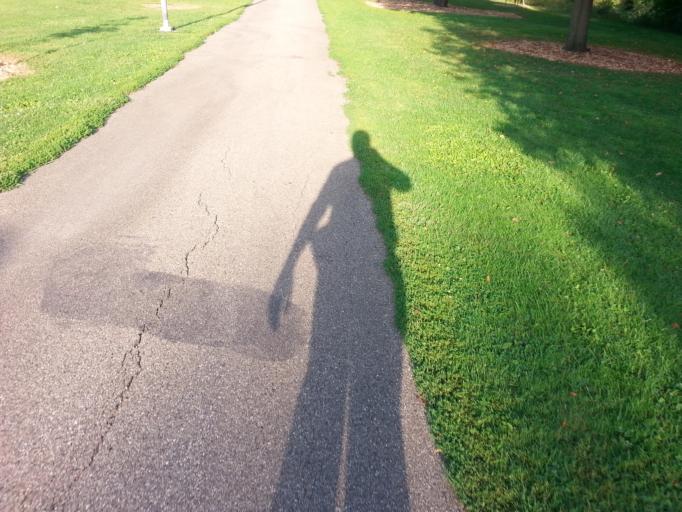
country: US
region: Minnesota
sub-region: Olmsted County
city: Rochester
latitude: 44.0261
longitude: -92.4811
